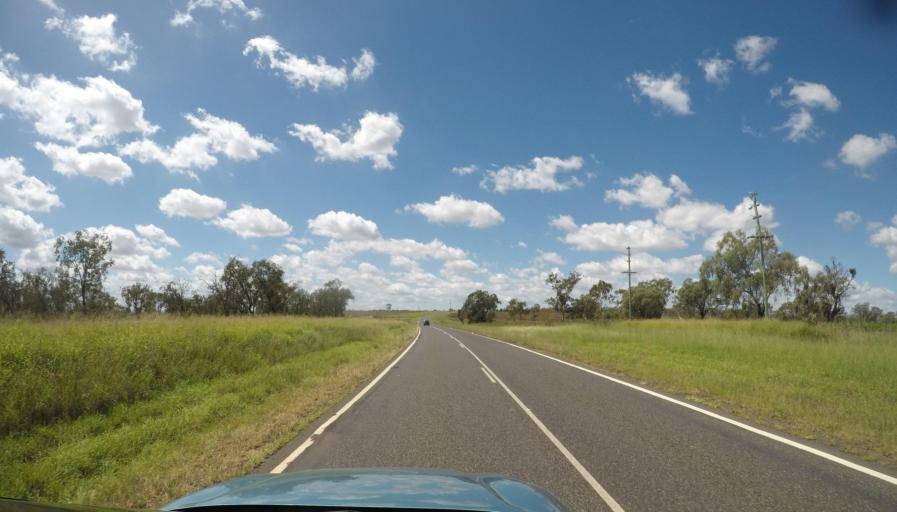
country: AU
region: Queensland
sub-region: Toowoomba
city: Oakey
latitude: -27.5549
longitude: 151.7052
